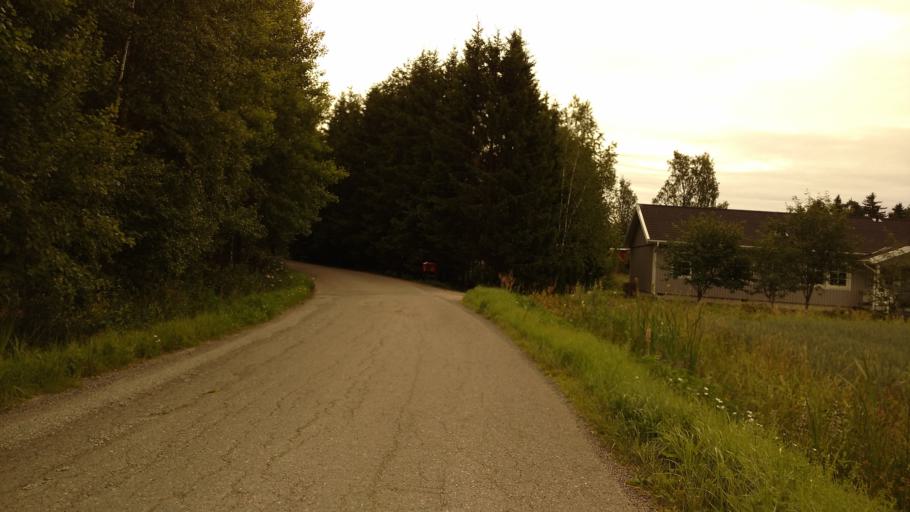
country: FI
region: Varsinais-Suomi
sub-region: Turku
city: Piikkioe
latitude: 60.4363
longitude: 22.4459
